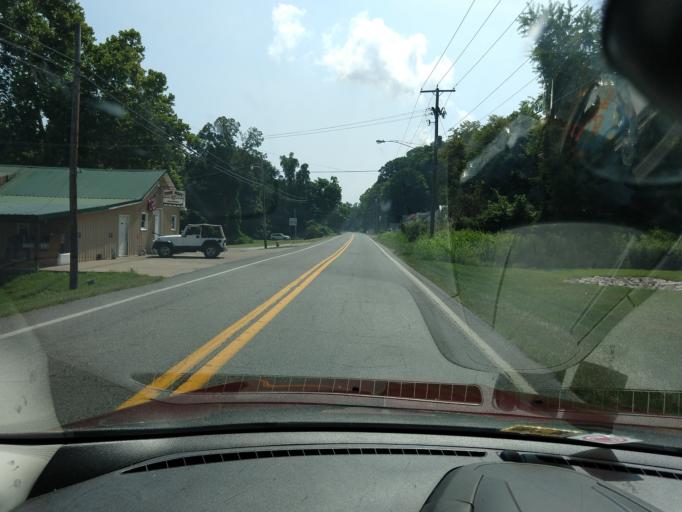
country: US
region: West Virginia
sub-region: Mason County
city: New Haven
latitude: 38.9851
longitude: -81.9638
